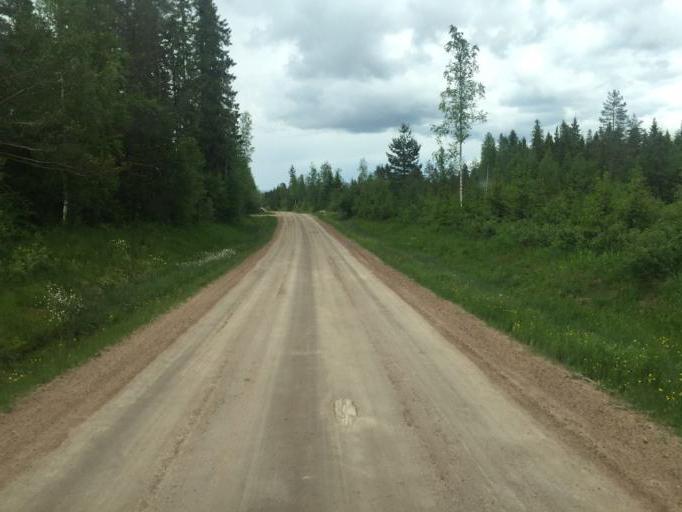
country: SE
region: Dalarna
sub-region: Malung-Saelens kommun
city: Malung
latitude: 60.4861
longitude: 13.7998
